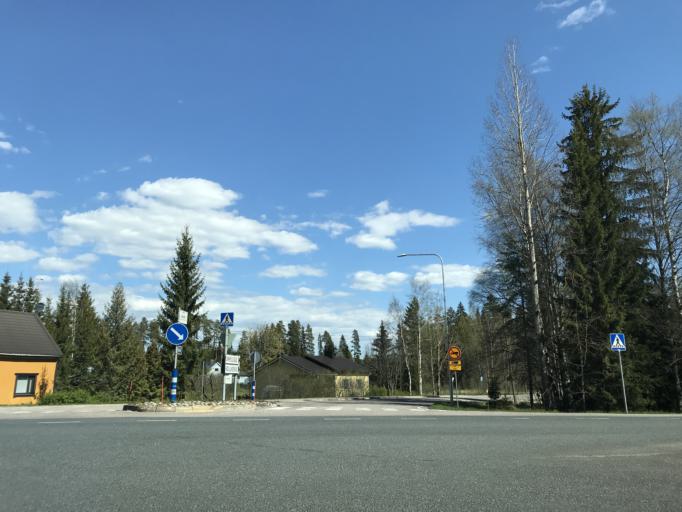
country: FI
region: Paijanne Tavastia
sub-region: Lahti
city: Orimattila
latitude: 60.8193
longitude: 25.7301
